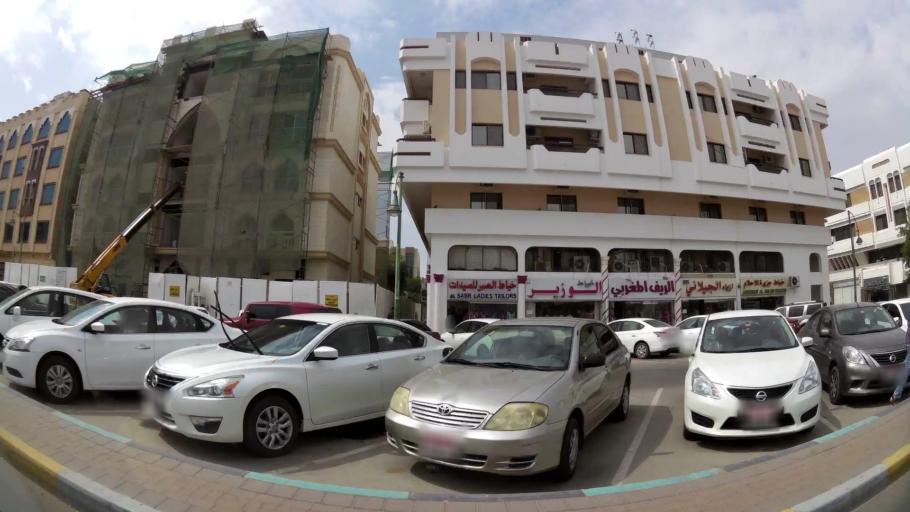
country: AE
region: Abu Dhabi
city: Al Ain
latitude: 24.2156
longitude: 55.7784
